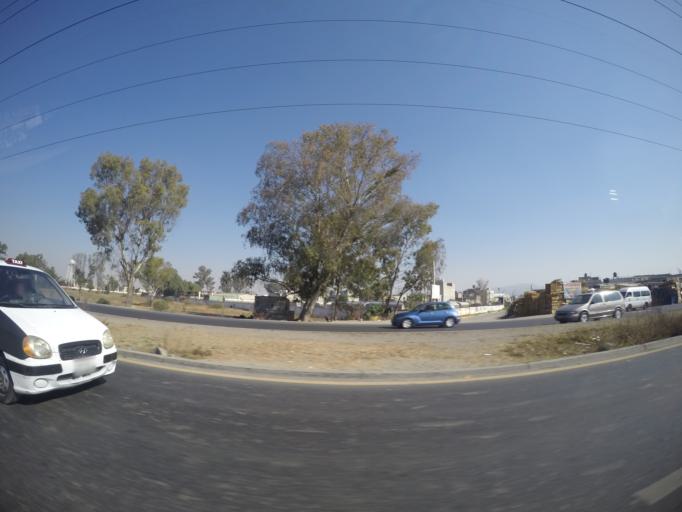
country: MX
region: Mexico
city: Santo Tomas Chiconautla
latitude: 19.6138
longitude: -99.0123
